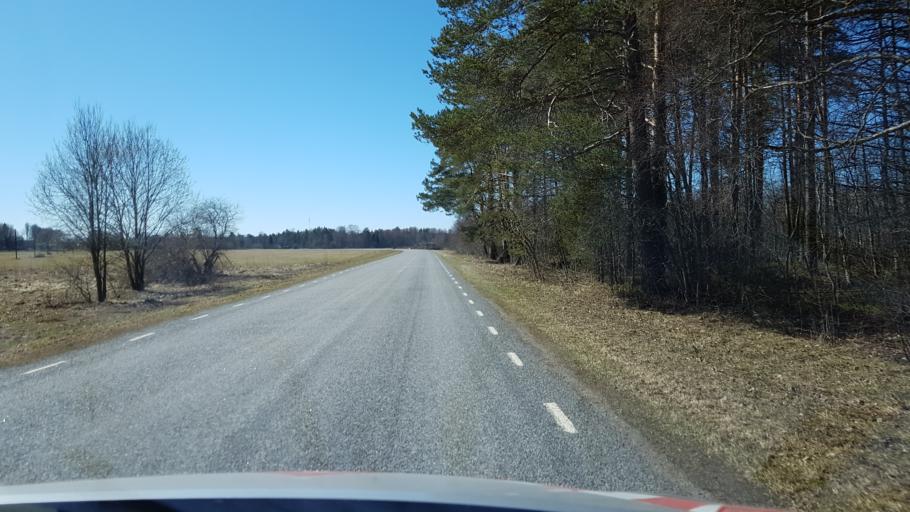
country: EE
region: Laeaene-Virumaa
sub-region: Haljala vald
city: Haljala
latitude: 59.4733
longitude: 26.2469
